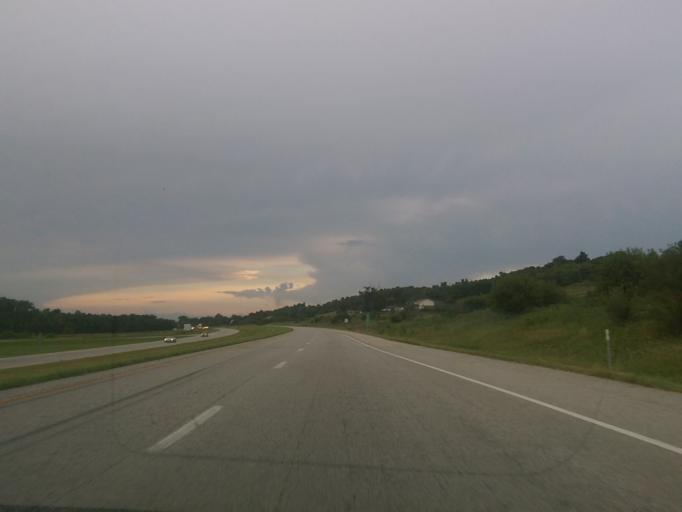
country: US
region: Missouri
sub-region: Holt County
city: Mound City
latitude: 40.1037
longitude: -95.2146
